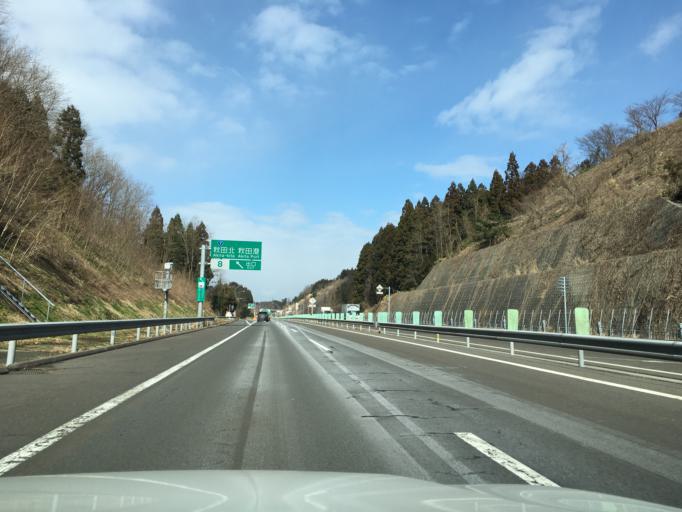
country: JP
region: Akita
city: Akita Shi
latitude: 39.7788
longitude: 140.1162
